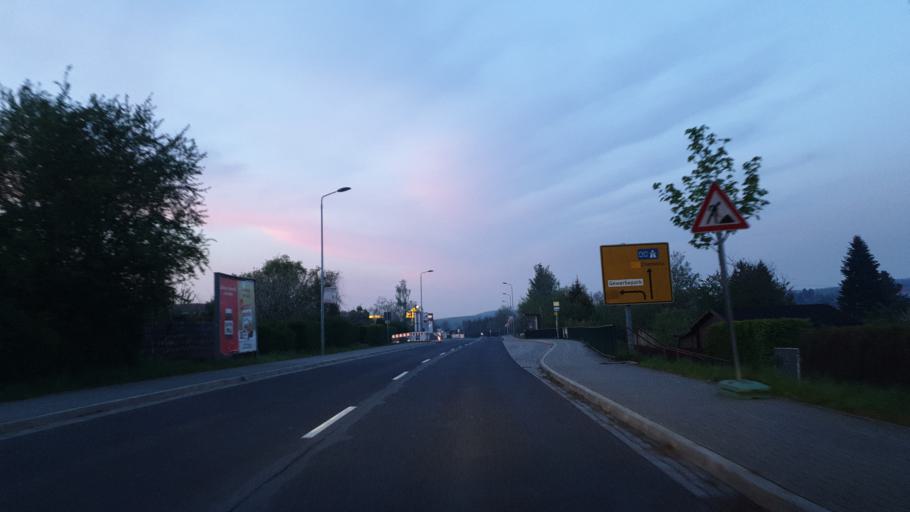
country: DE
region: Saxony
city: Stollberg
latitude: 50.7143
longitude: 12.7813
